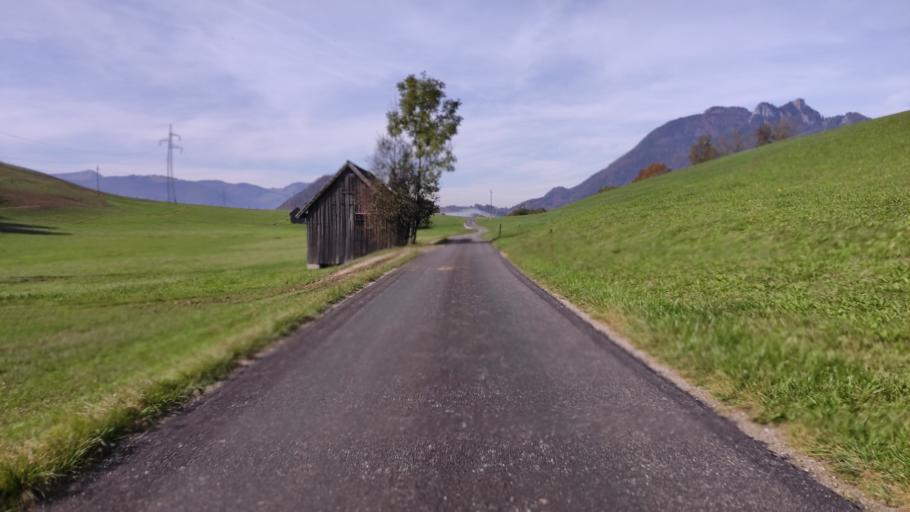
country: AT
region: Salzburg
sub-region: Politischer Bezirk Salzburg-Umgebung
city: Strobl
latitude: 47.7221
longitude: 13.5200
